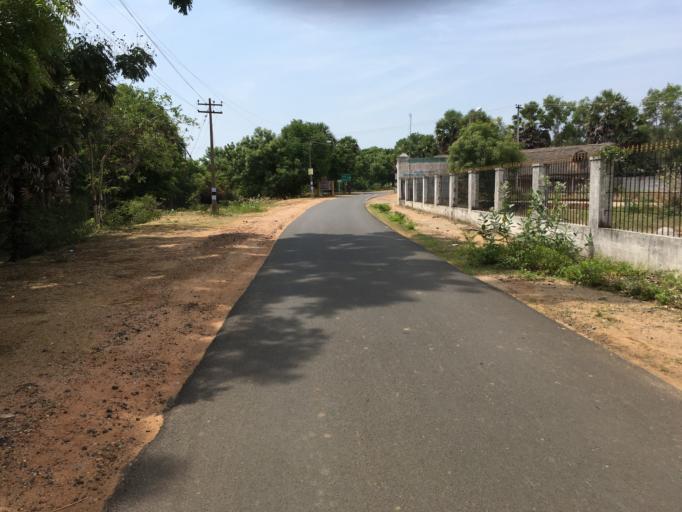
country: IN
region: Tamil Nadu
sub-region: Villupuram
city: Auroville
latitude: 12.0047
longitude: 79.7977
